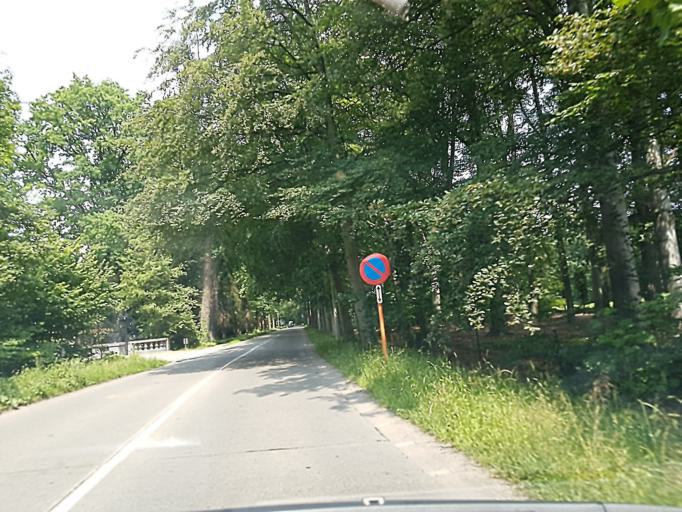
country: BE
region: Flanders
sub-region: Provincie Antwerpen
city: Wijnegem
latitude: 51.2344
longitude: 4.5352
